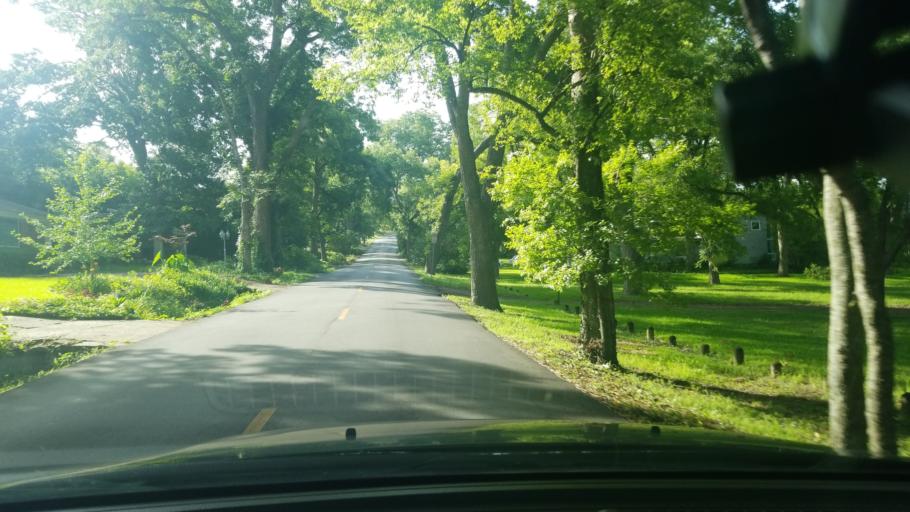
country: US
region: Texas
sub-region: Dallas County
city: Highland Park
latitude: 32.8099
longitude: -96.7075
